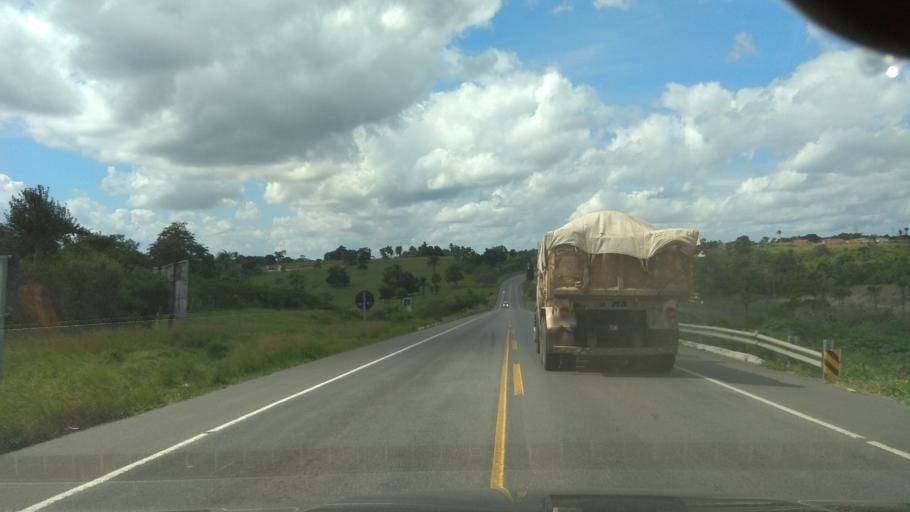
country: BR
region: Bahia
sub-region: Cachoeira
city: Cachoeira
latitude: -12.5967
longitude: -39.0353
